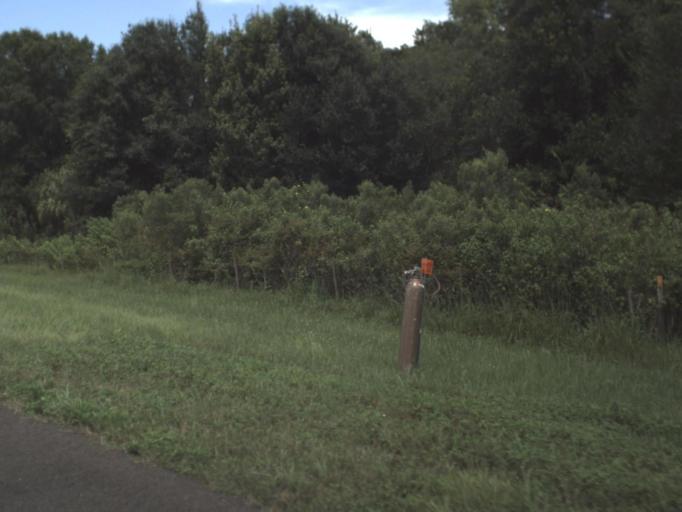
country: US
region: Florida
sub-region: Pasco County
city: Wesley Chapel
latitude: 28.2153
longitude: -82.3532
